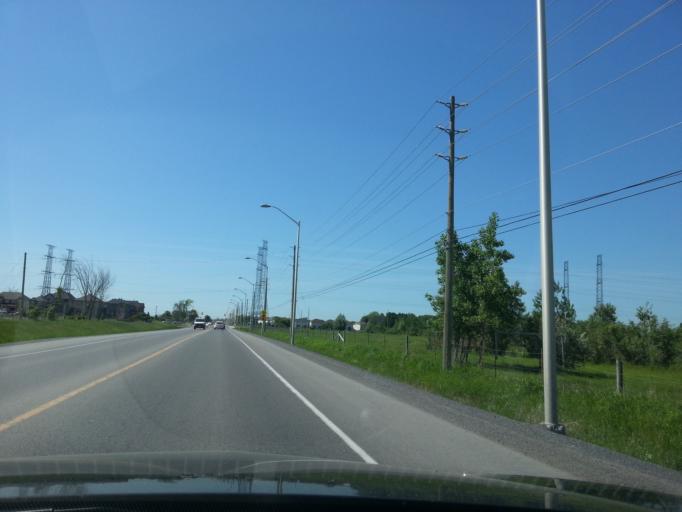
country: CA
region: Ontario
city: Bells Corners
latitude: 45.2781
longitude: -75.8773
